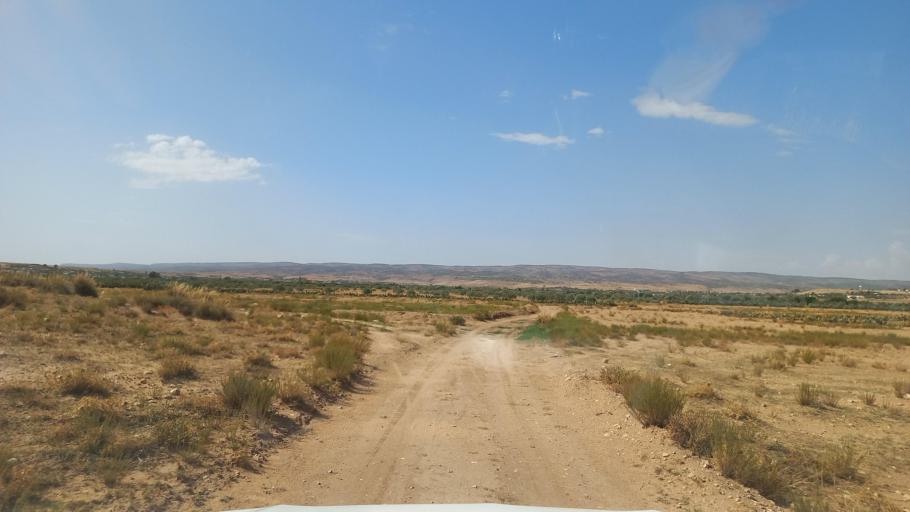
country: TN
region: Al Qasrayn
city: Kasserine
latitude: 35.2558
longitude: 8.9555
